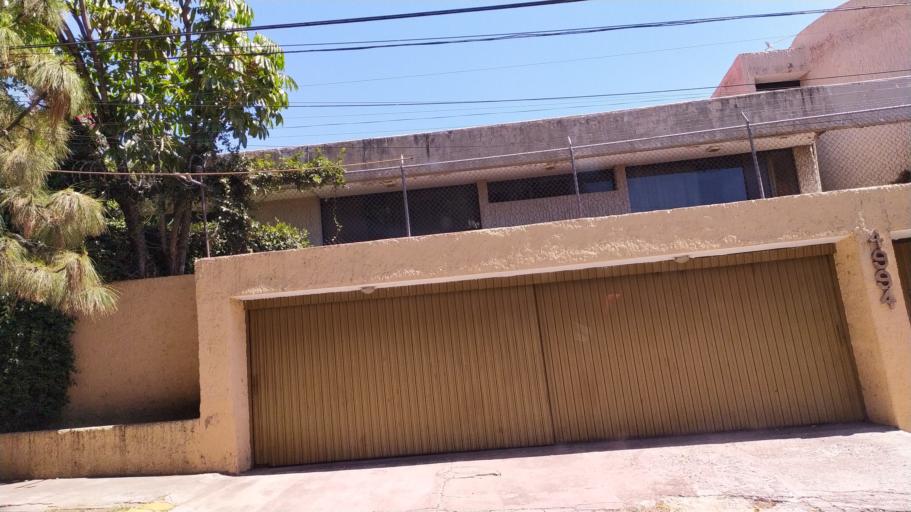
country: MX
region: Jalisco
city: Zapopan2
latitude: 20.6884
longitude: -103.4178
